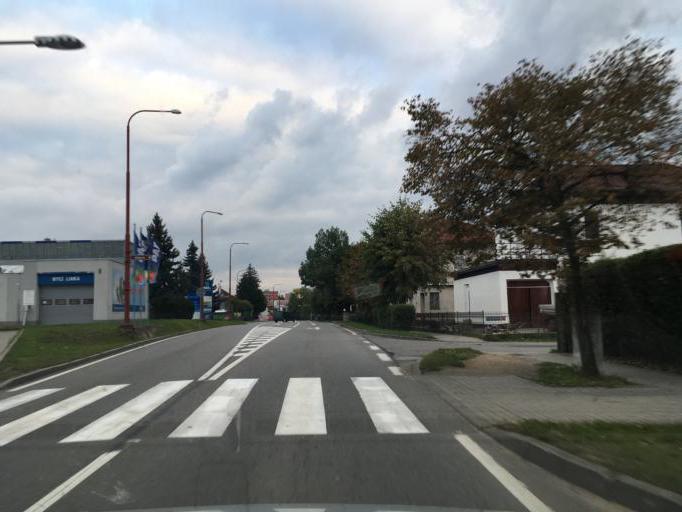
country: CZ
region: Vysocina
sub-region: Okres Trebic
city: Trebic
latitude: 49.2100
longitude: 15.8578
